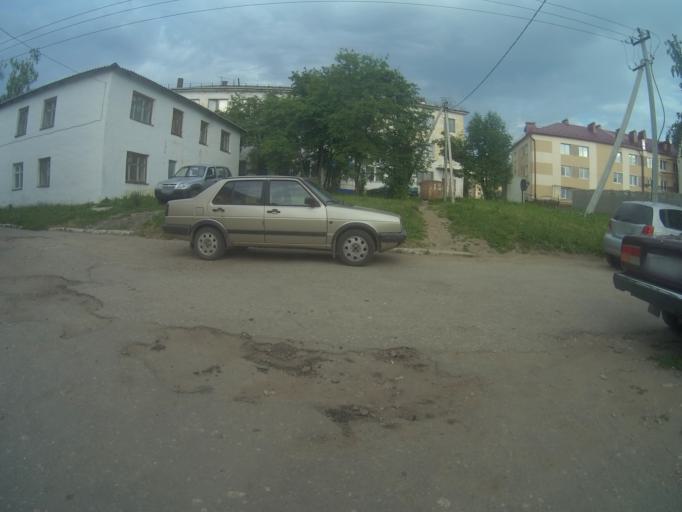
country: RU
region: Vladimir
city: Vladimir
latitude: 56.2234
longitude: 40.4084
